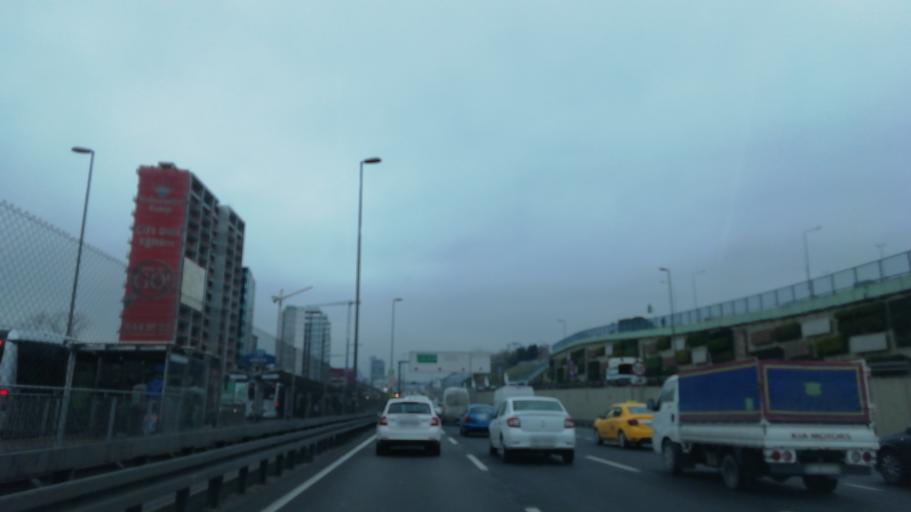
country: TR
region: Istanbul
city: guengoeren merter
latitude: 41.0074
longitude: 28.8972
